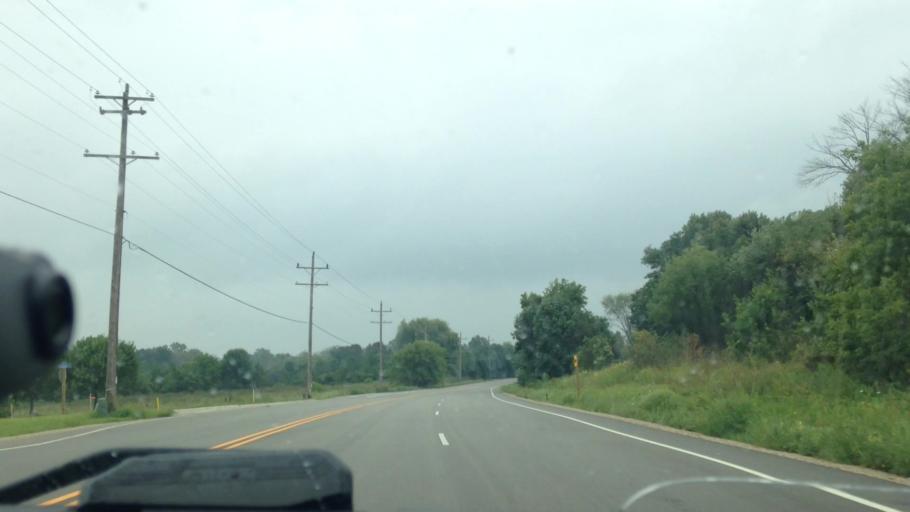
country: US
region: Wisconsin
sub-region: Washington County
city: Richfield
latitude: 43.3020
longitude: -88.2323
